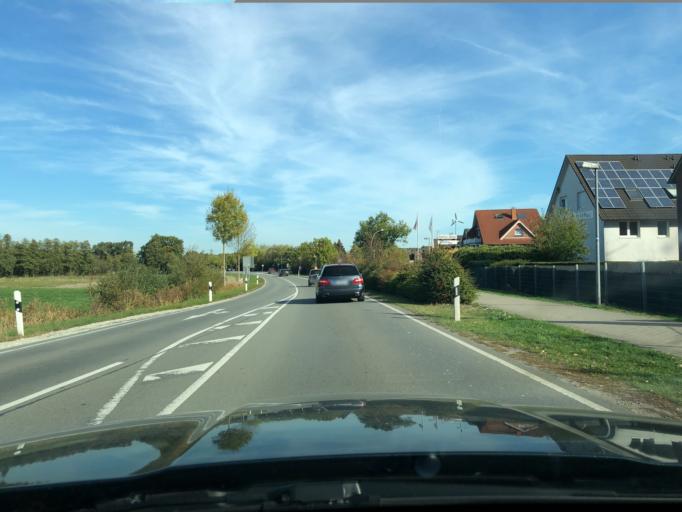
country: DE
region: Lower Saxony
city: Hasbergen
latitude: 52.2387
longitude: 7.9673
